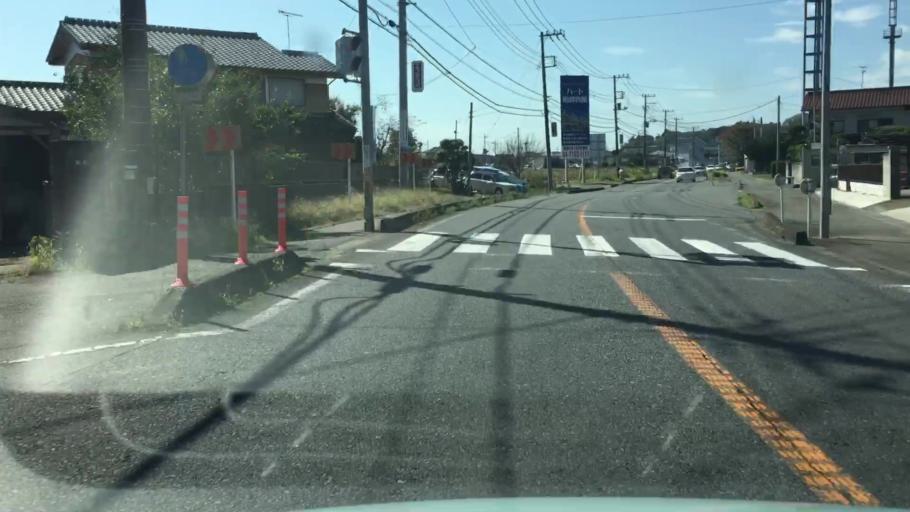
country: JP
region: Ibaraki
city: Ryugasaki
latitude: 35.8631
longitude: 140.1533
